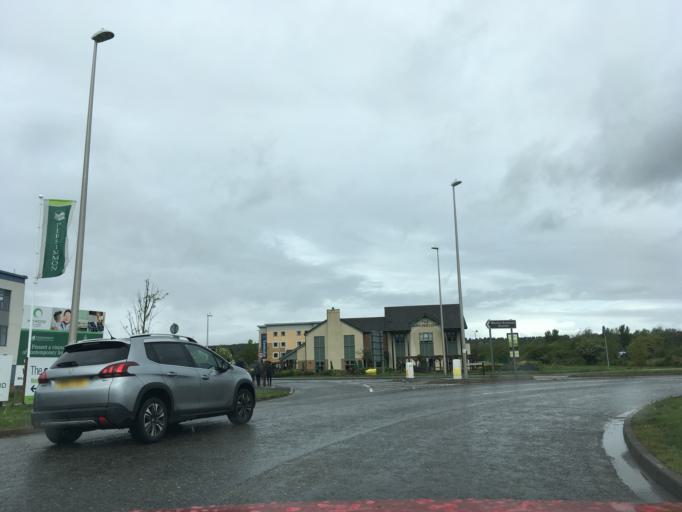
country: GB
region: England
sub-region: North Somerset
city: Hutton
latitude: 51.3416
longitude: -2.9323
